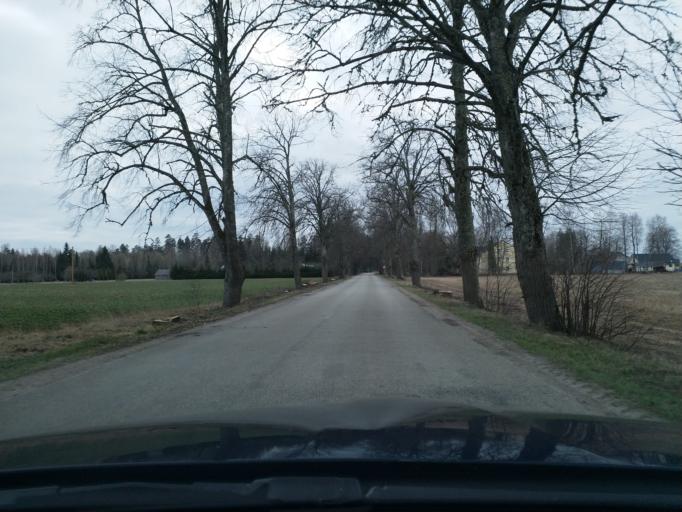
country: LV
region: Talsu Rajons
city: Sabile
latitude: 56.9373
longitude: 22.5869
